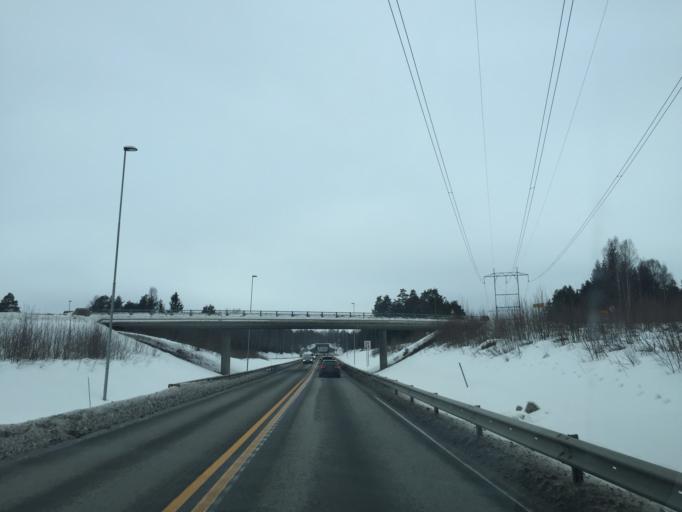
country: NO
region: Hedmark
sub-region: Loten
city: Loten
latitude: 60.7862
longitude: 11.3033
